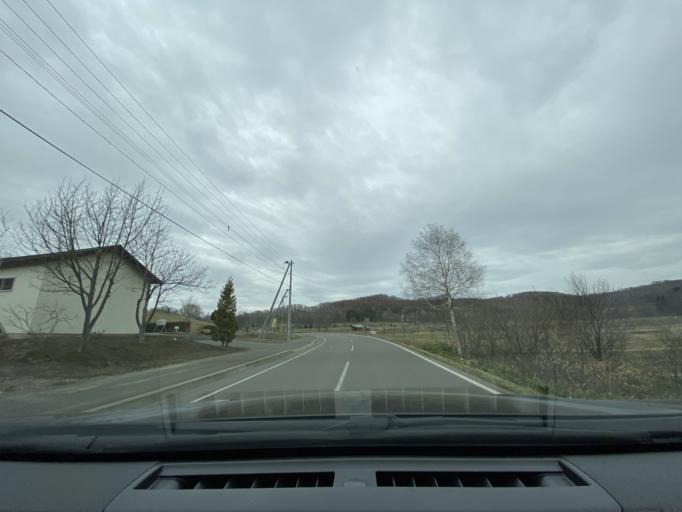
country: JP
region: Hokkaido
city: Nayoro
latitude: 44.0929
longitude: 142.4244
